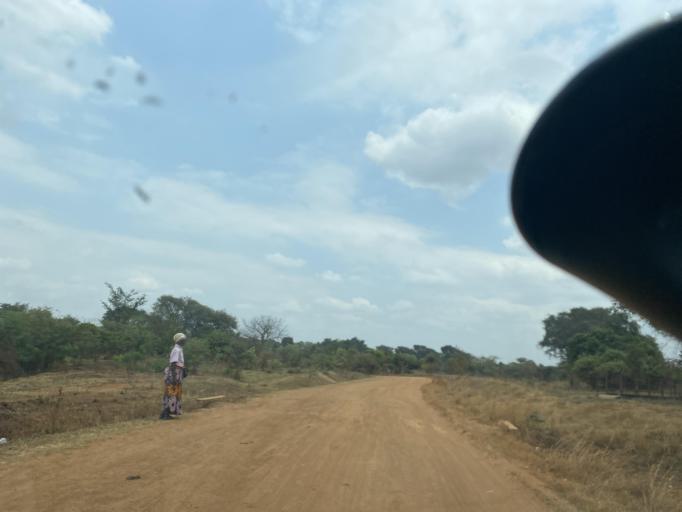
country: ZM
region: Lusaka
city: Chongwe
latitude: -15.5085
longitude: 28.8182
